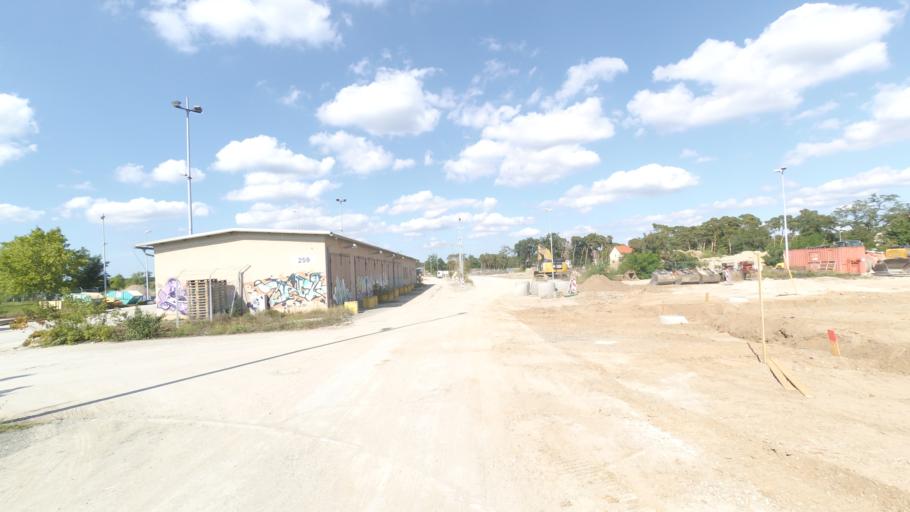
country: DE
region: Hesse
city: Viernheim
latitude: 49.5200
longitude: 8.5362
